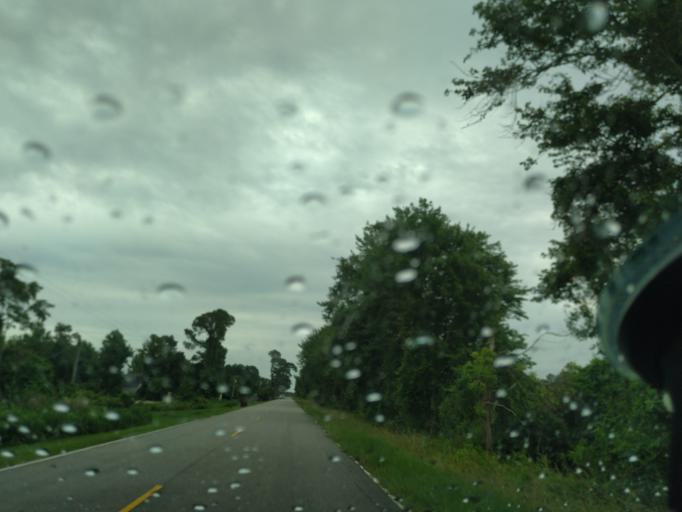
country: US
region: North Carolina
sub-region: Beaufort County
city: Belhaven
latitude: 35.7625
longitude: -76.5219
